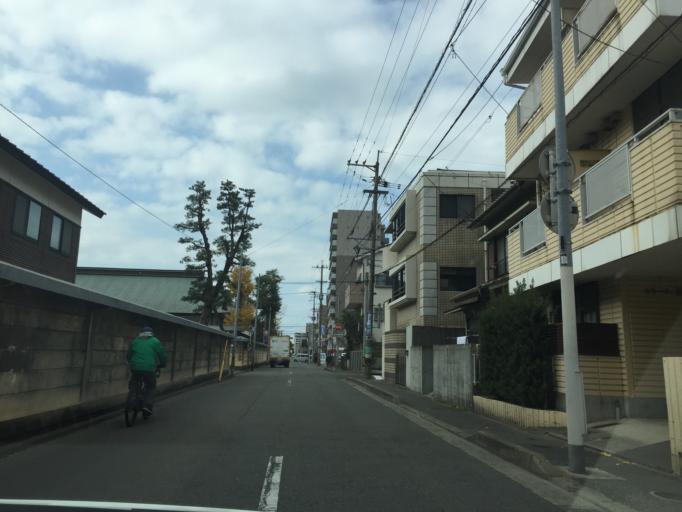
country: JP
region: Fukuoka
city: Fukuoka-shi
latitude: 33.6150
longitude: 130.4238
